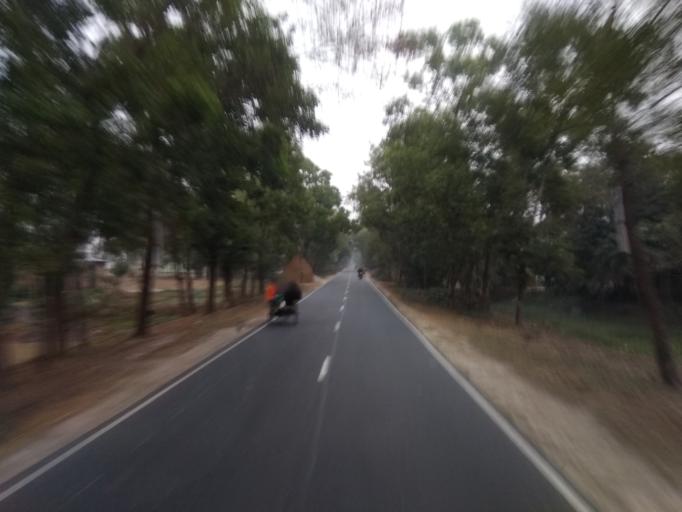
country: BD
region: Rajshahi
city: Bogra
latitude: 24.6533
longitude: 89.2606
